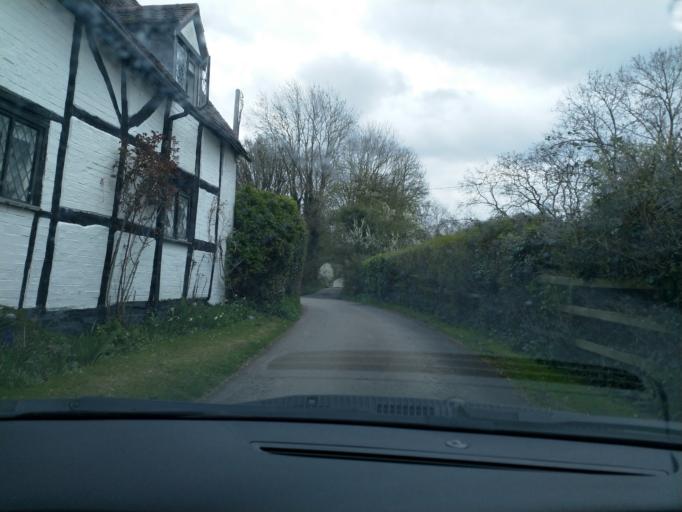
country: GB
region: England
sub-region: Warwickshire
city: Henley in Arden
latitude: 52.2936
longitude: -1.7289
